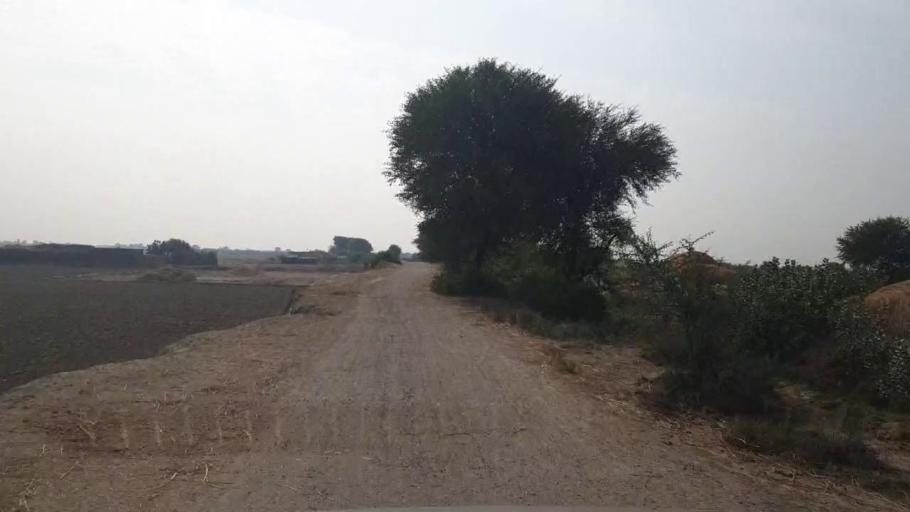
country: PK
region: Sindh
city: Tando Muhammad Khan
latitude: 25.1253
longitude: 68.4916
